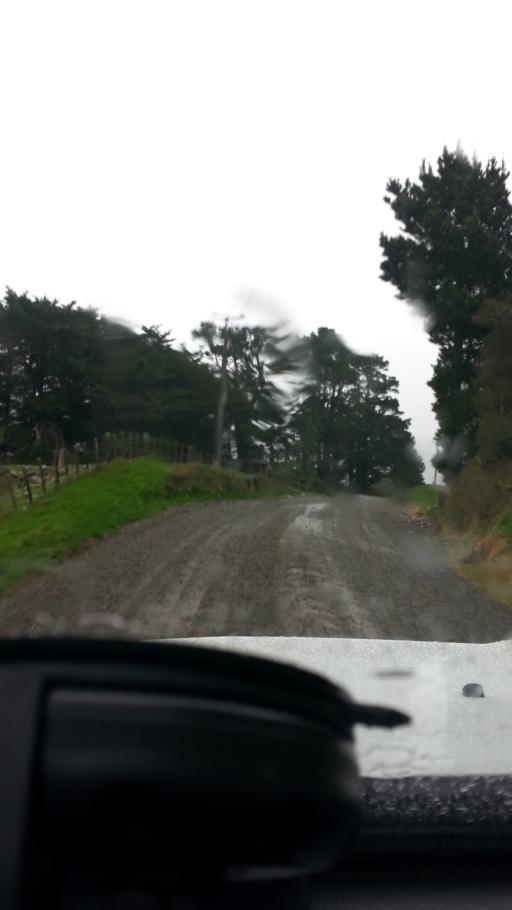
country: NZ
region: Wellington
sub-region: Masterton District
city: Masterton
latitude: -40.8895
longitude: 175.5294
